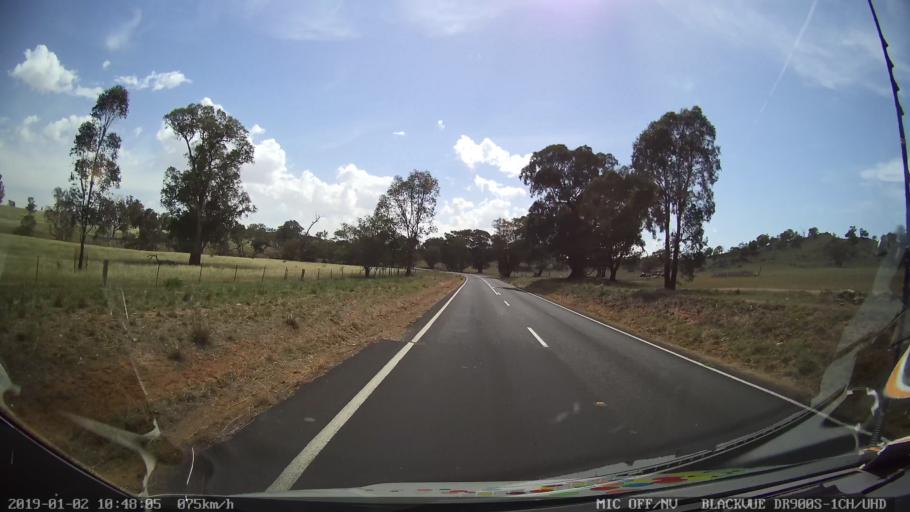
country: AU
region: New South Wales
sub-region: Cootamundra
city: Cootamundra
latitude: -34.7394
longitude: 148.2750
